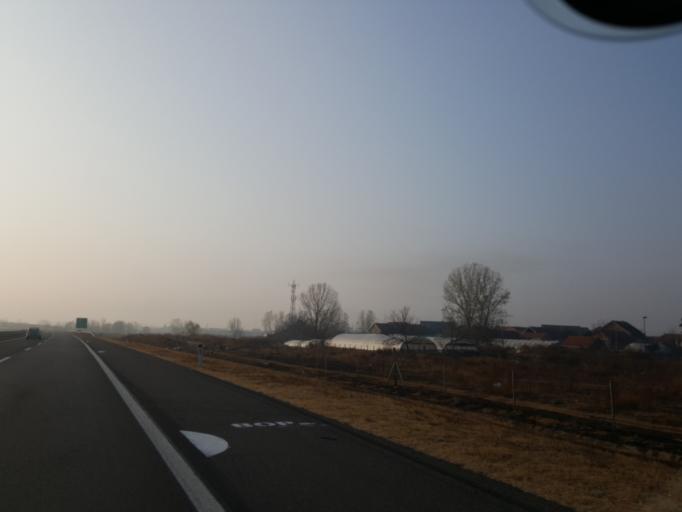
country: RS
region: Central Serbia
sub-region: Jablanicki Okrug
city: Leskovac
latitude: 42.9881
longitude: 22.0276
